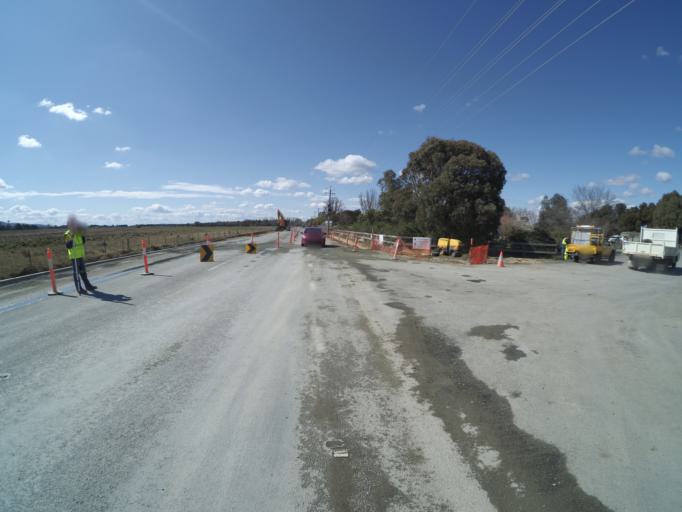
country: AU
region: New South Wales
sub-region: Palerang
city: Bungendore
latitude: -35.2629
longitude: 149.4342
